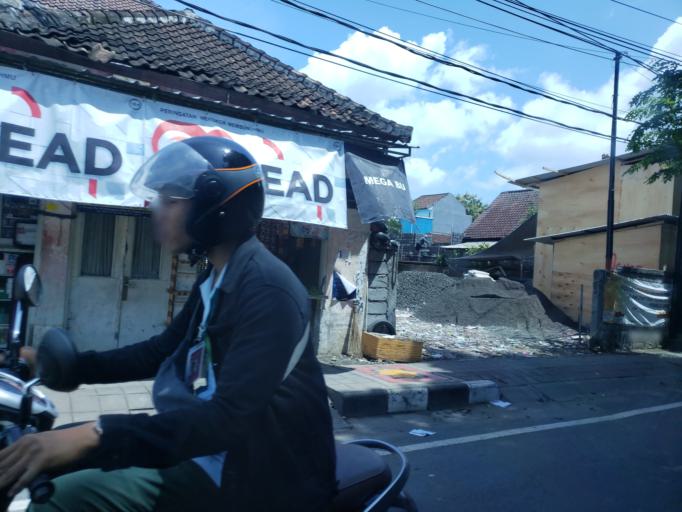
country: ID
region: Bali
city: Kelanabian
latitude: -8.7546
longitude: 115.1775
